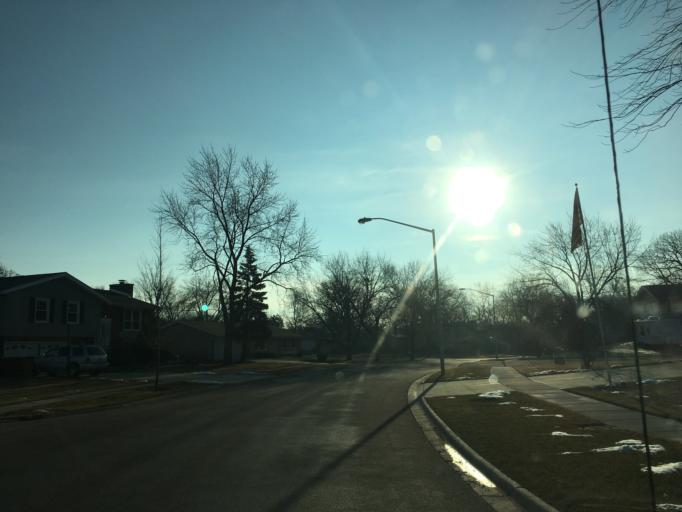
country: US
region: Illinois
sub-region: Cook County
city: Schaumburg
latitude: 42.0258
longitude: -88.0968
